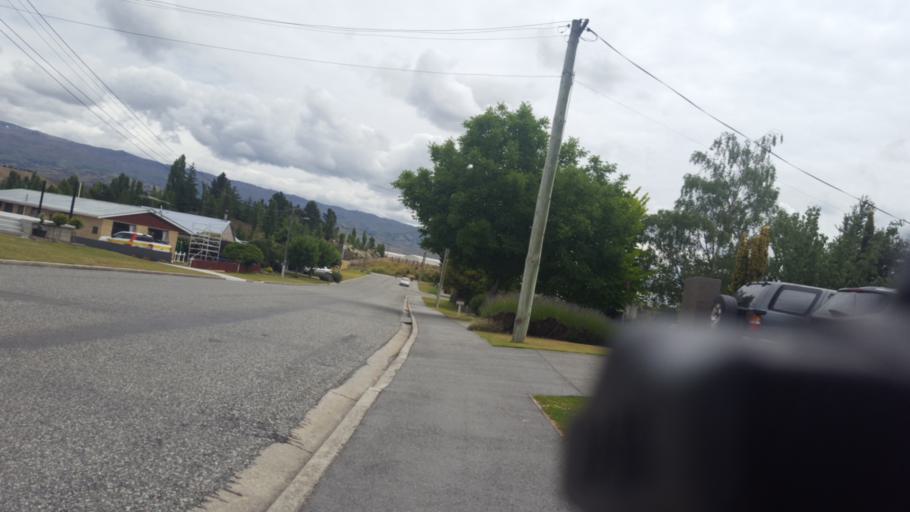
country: NZ
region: Otago
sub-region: Queenstown-Lakes District
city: Wanaka
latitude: -45.2494
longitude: 169.3788
